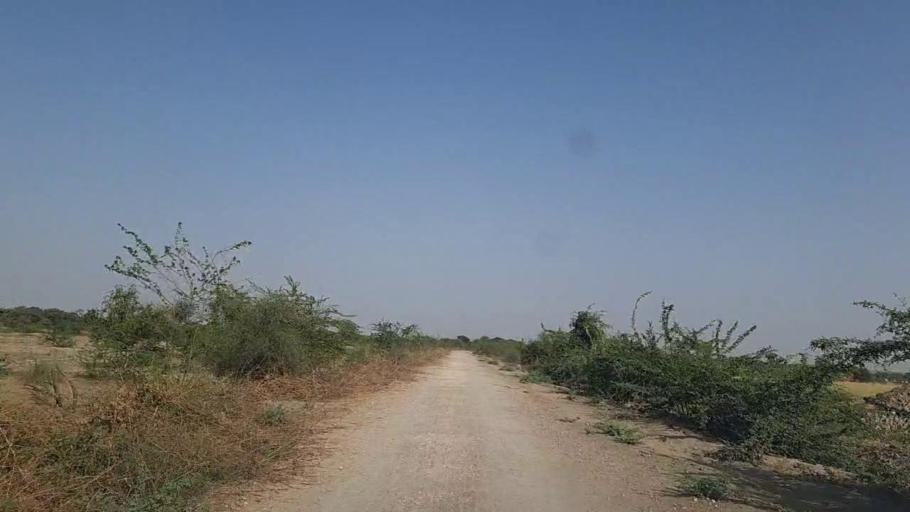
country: PK
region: Sindh
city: Naukot
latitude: 24.6098
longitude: 69.2793
